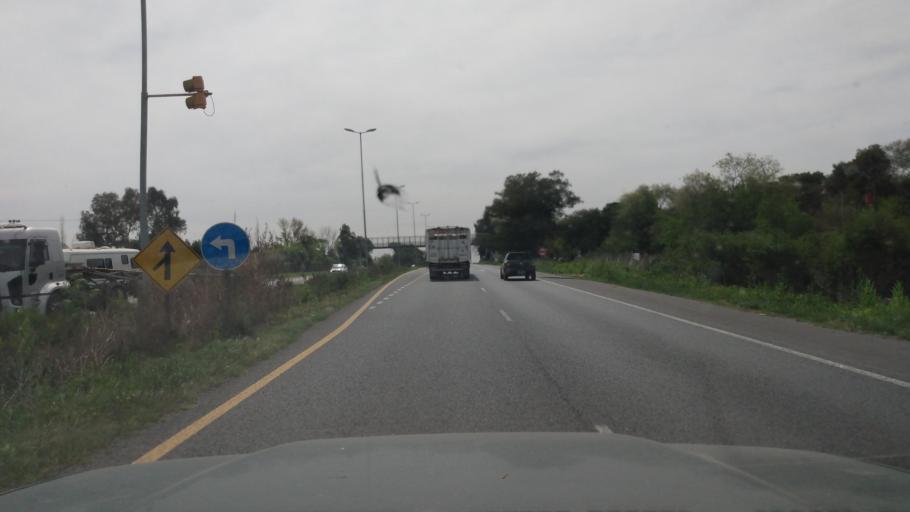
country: AR
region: Buenos Aires
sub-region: Partido de Lujan
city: Lujan
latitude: -34.4488
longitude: -59.0530
